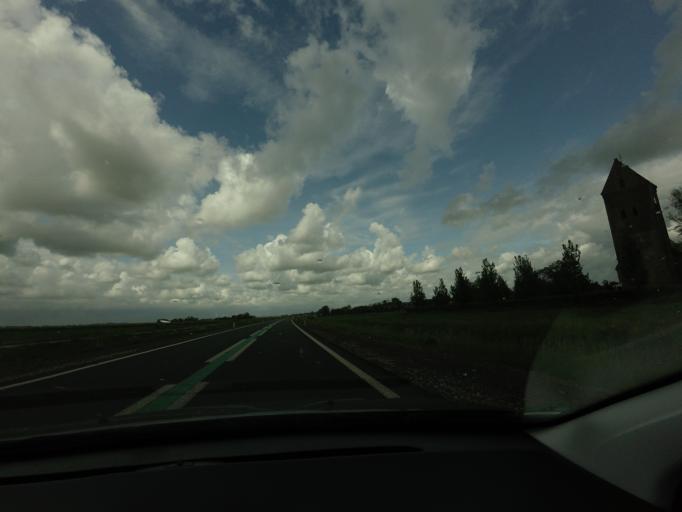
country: NL
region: Friesland
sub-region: Sudwest Fryslan
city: Workum
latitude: 53.0187
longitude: 5.4764
